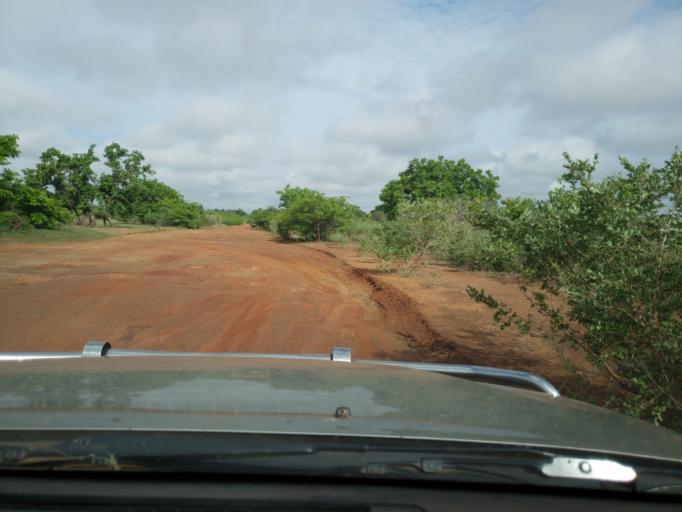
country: ML
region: Sikasso
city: Koutiala
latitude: 12.3924
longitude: -5.9964
